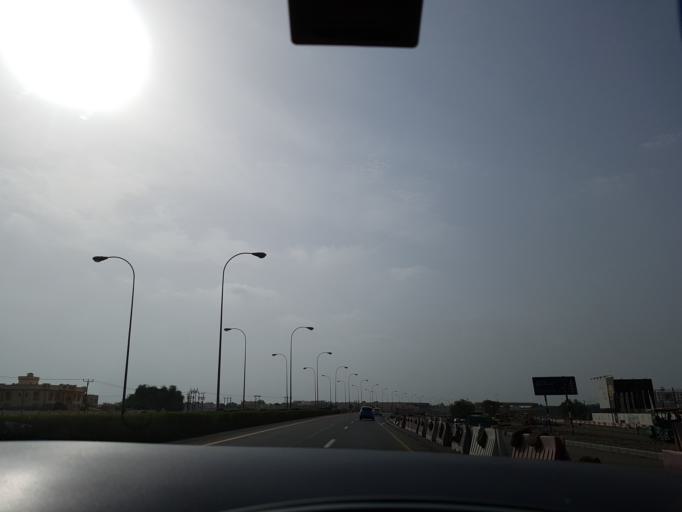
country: OM
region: Al Batinah
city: Al Sohar
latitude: 24.3901
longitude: 56.6967
